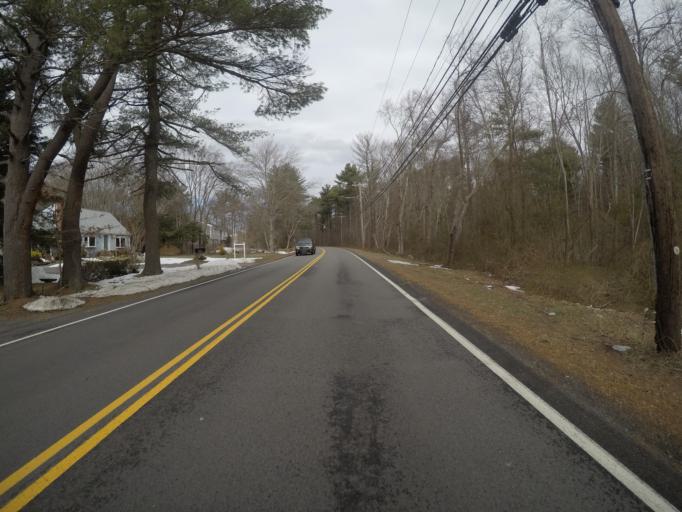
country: US
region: Massachusetts
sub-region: Bristol County
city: Easton
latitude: 42.0483
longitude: -71.1276
